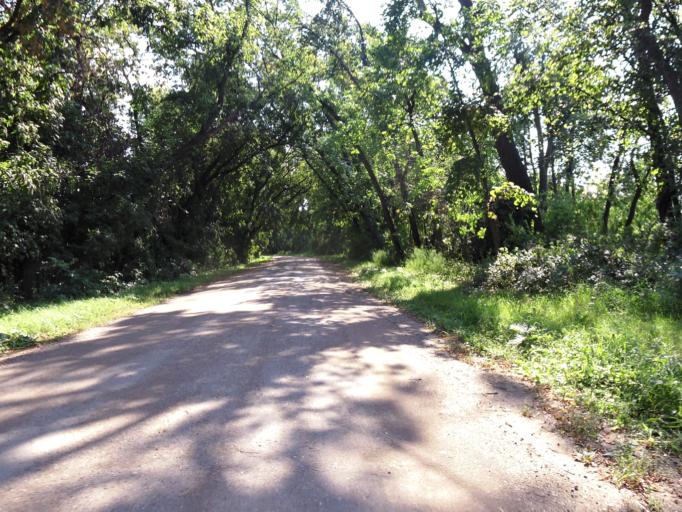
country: US
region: North Dakota
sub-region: Walsh County
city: Grafton
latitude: 48.4257
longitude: -97.4011
